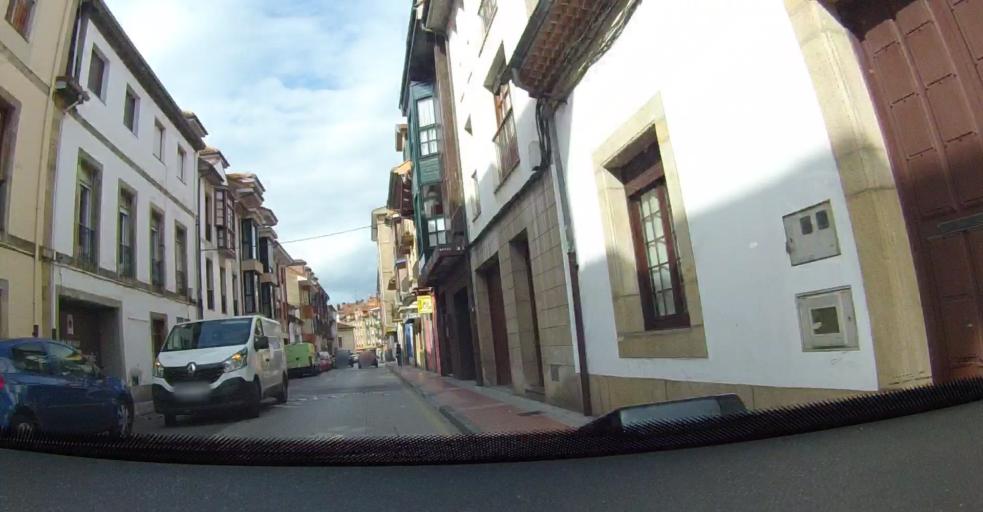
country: ES
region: Asturias
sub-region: Province of Asturias
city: Villaviciosa
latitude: 43.4796
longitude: -5.4356
